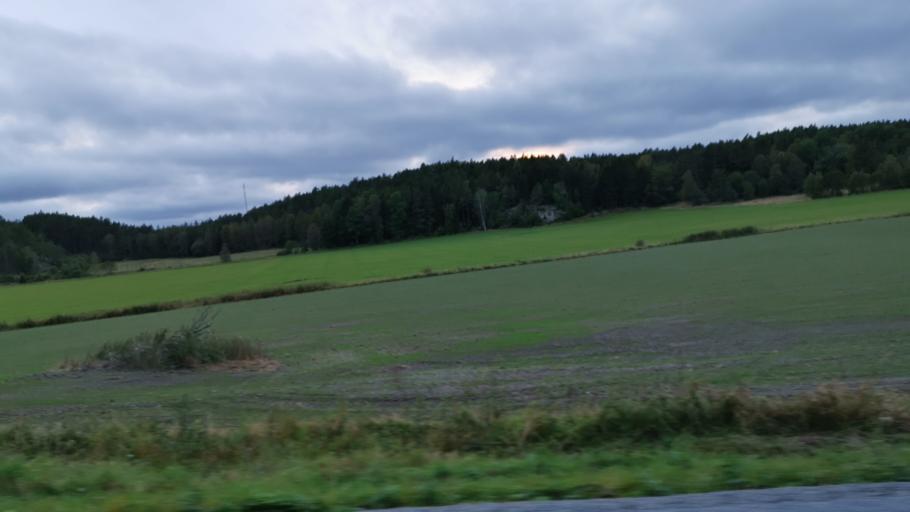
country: SE
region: Vaestra Goetaland
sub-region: Tanums Kommun
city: Tanumshede
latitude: 58.6840
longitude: 11.3364
